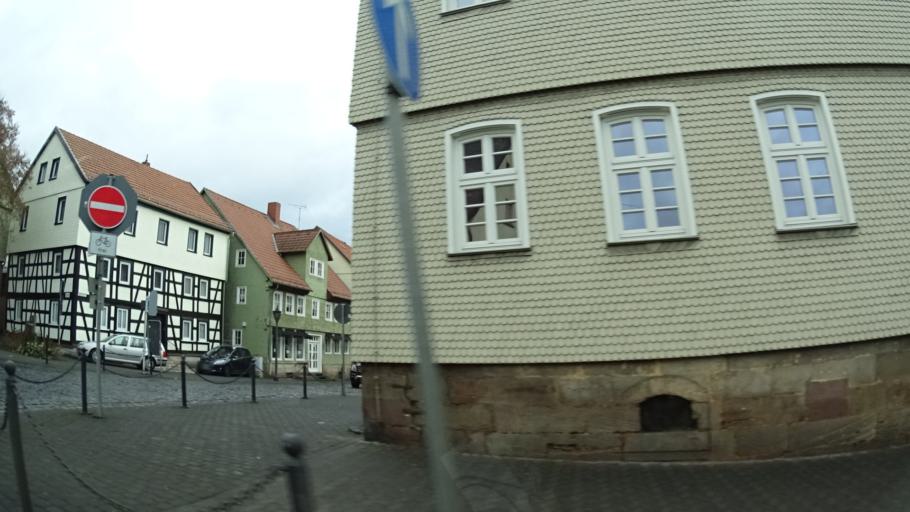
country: DE
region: Hesse
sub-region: Regierungsbezirk Giessen
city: Lauterbach
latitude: 50.6374
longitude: 9.3940
